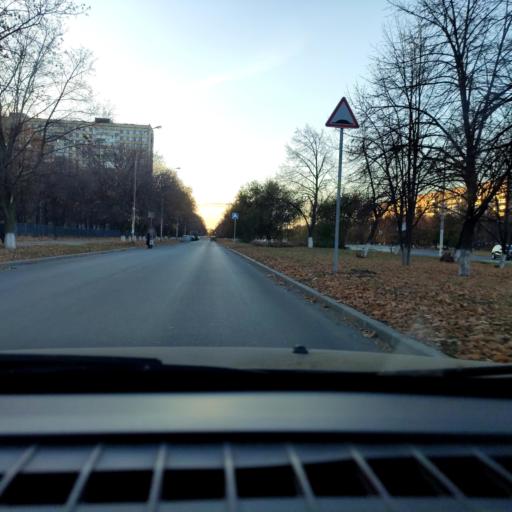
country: RU
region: Samara
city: Tol'yatti
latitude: 53.5203
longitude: 49.2700
